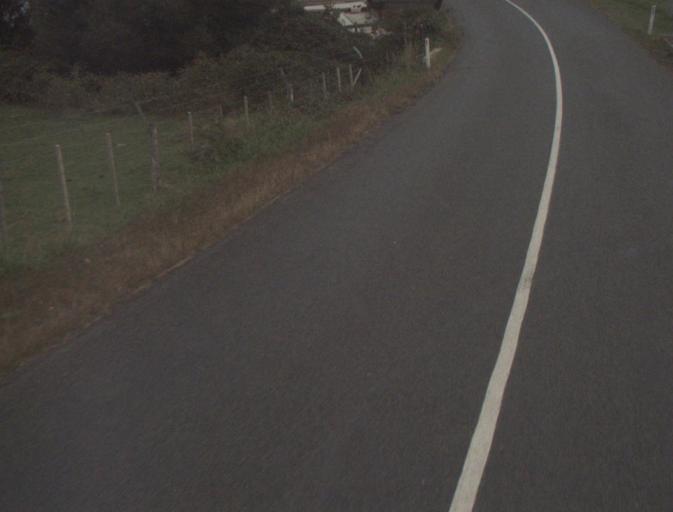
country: AU
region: Tasmania
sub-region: Launceston
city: Newstead
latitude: -41.5017
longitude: 147.1948
